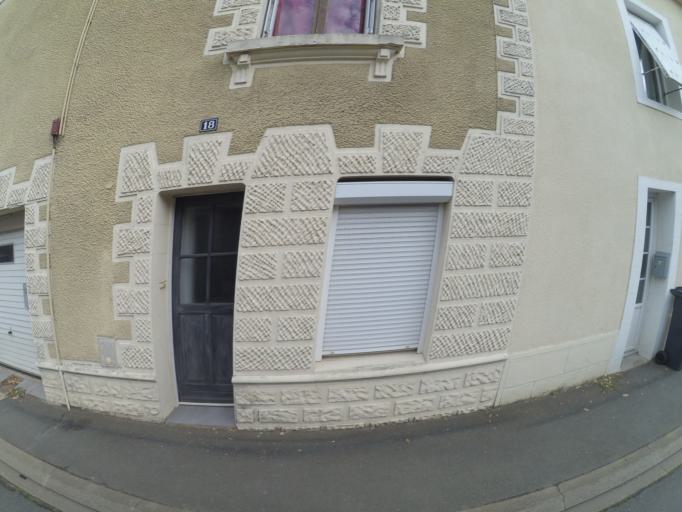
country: FR
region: Pays de la Loire
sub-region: Departement de Maine-et-Loire
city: Jallais
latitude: 47.1958
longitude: -0.8655
